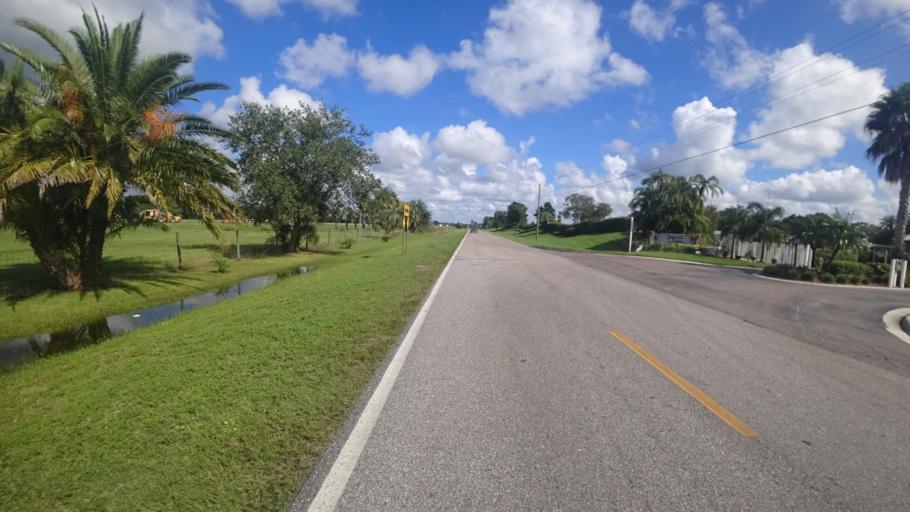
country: US
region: Florida
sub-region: Manatee County
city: Ellenton
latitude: 27.5897
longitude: -82.5109
